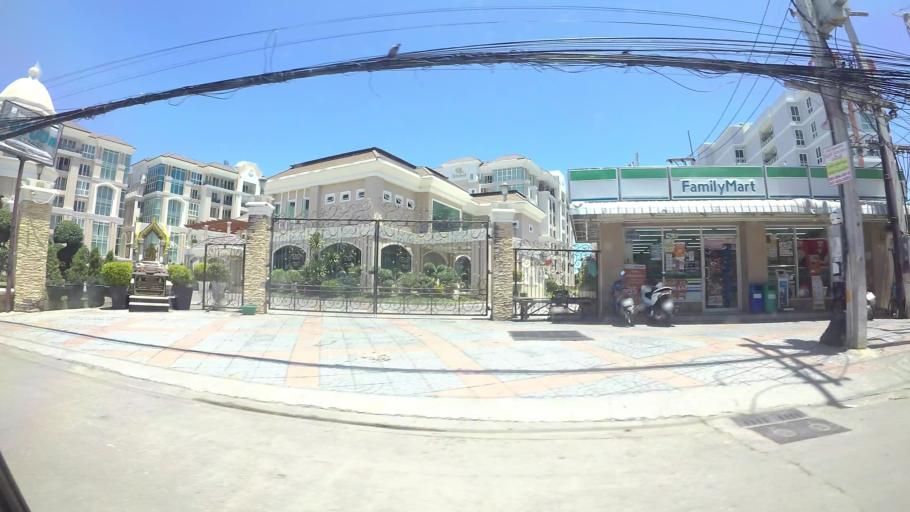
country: TH
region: Chon Buri
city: Phatthaya
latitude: 12.9284
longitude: 100.8952
